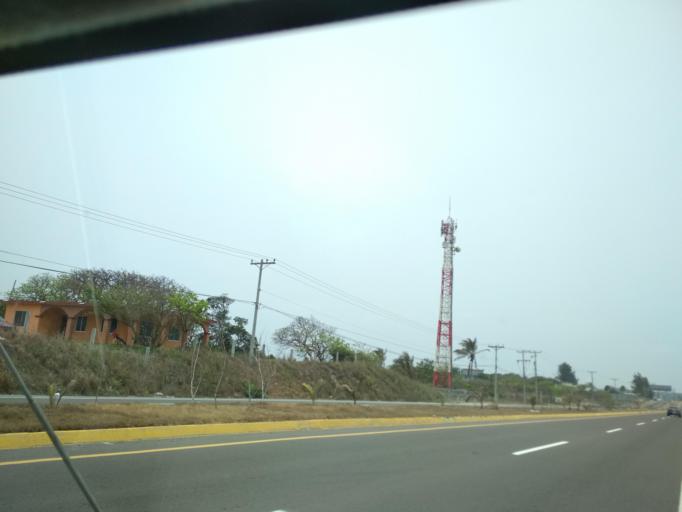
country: MX
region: Veracruz
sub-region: Alvarado
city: Playa de la Libertad
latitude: 19.0560
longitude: -96.0540
